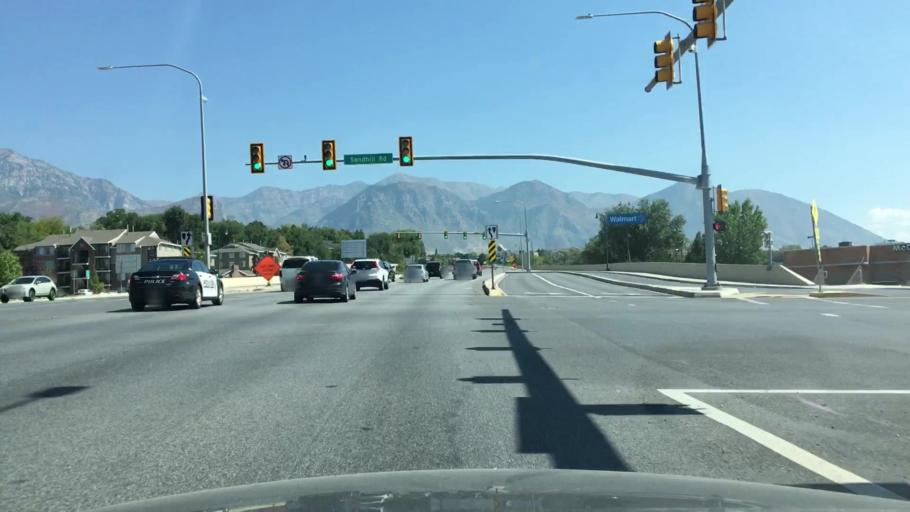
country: US
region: Utah
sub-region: Utah County
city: Orem
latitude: 40.2750
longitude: -111.7136
